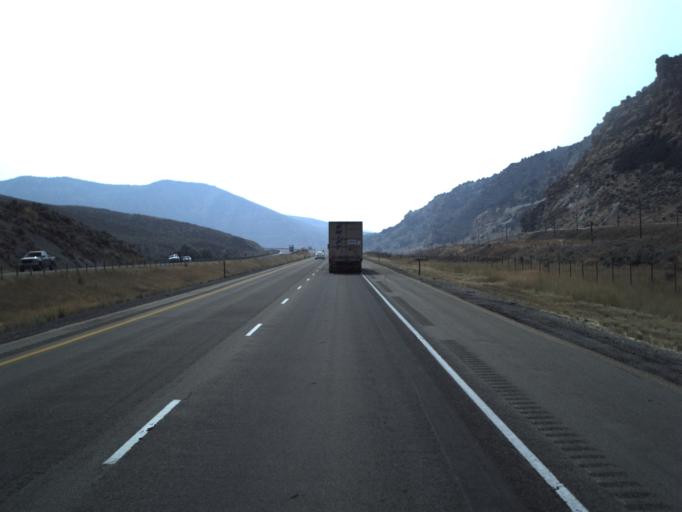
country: US
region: Utah
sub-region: Summit County
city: Coalville
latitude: 41.0618
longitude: -111.2855
